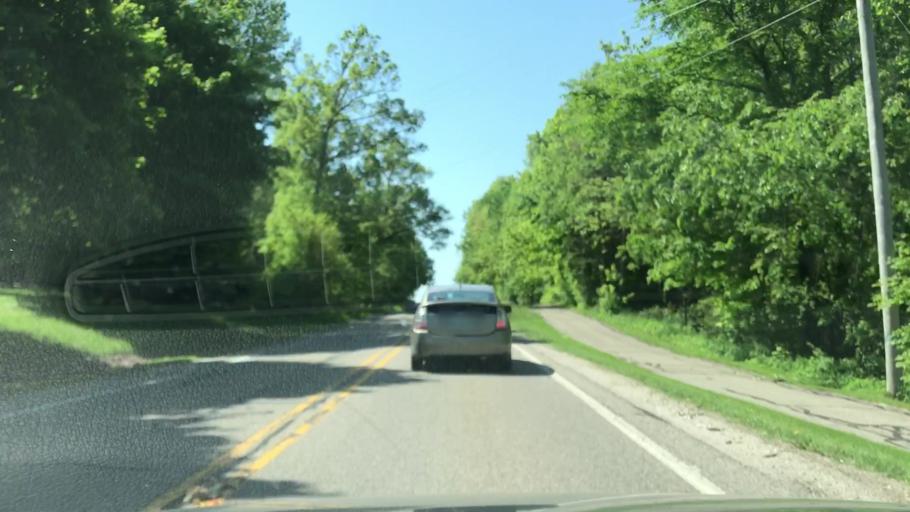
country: US
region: Michigan
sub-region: Kent County
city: Forest Hills
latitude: 42.9242
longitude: -85.5400
